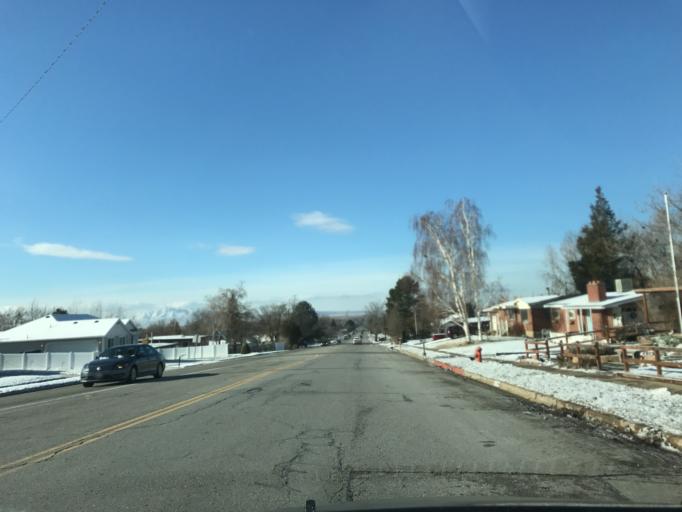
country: US
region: Utah
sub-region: Davis County
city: Kaysville
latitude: 41.0380
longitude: -111.9250
